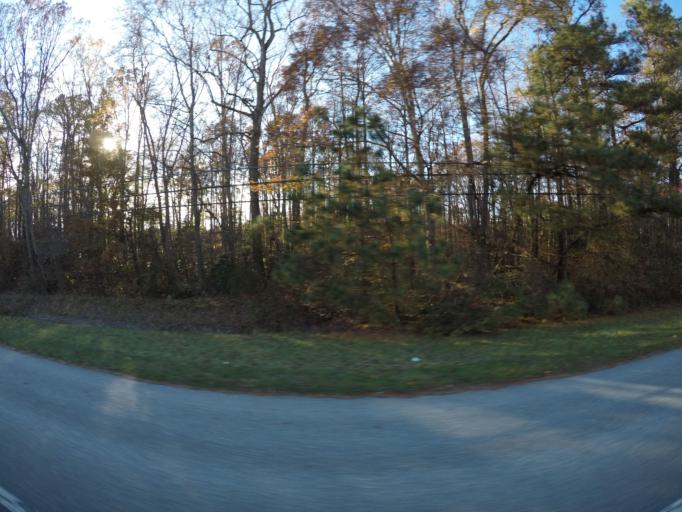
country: US
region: Maryland
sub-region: Saint Mary's County
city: Leonardtown
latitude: 38.3399
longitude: -76.6758
